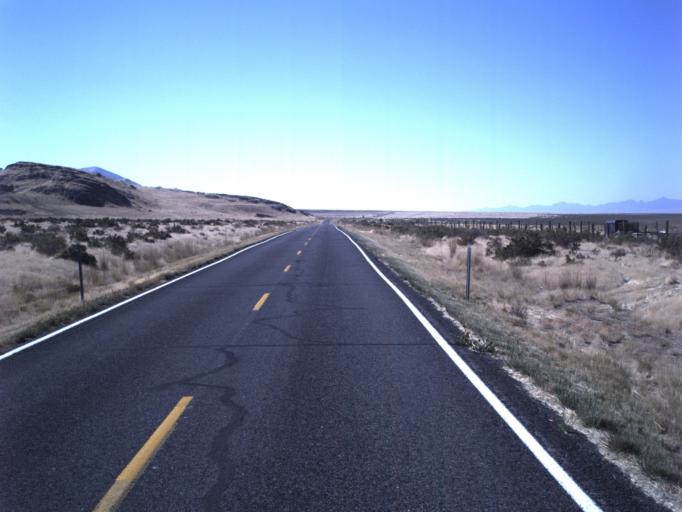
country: US
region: Utah
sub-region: Tooele County
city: Grantsville
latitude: 40.6197
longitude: -112.7011
